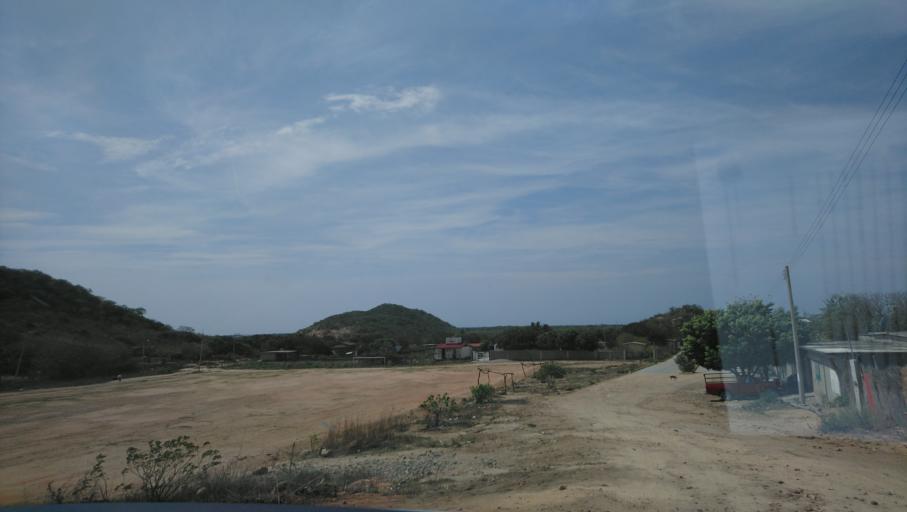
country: MX
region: Oaxaca
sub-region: Salina Cruz
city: Salina Cruz
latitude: 16.2139
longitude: -95.1253
